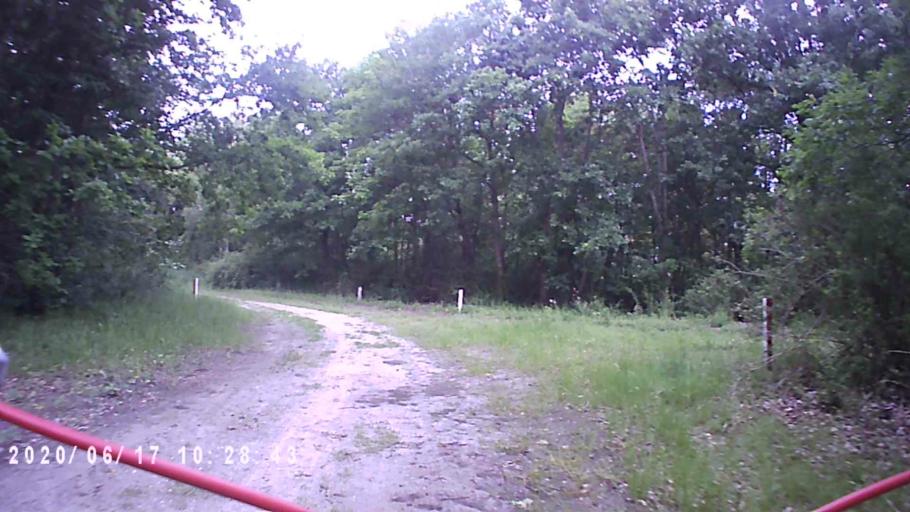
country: NL
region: Groningen
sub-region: Gemeente De Marne
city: Ulrum
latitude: 53.3963
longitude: 6.2413
